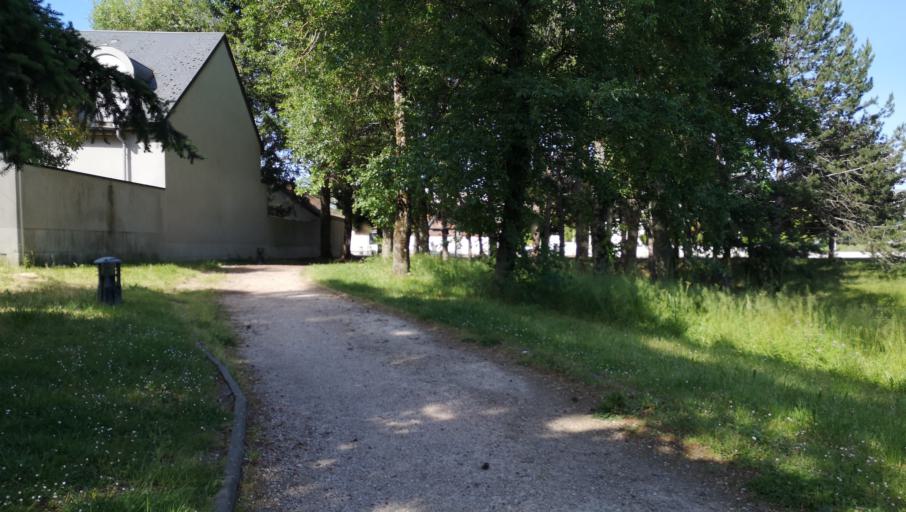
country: FR
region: Centre
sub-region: Departement du Loiret
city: Saint-Jean-de-Braye
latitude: 47.9142
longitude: 1.9790
